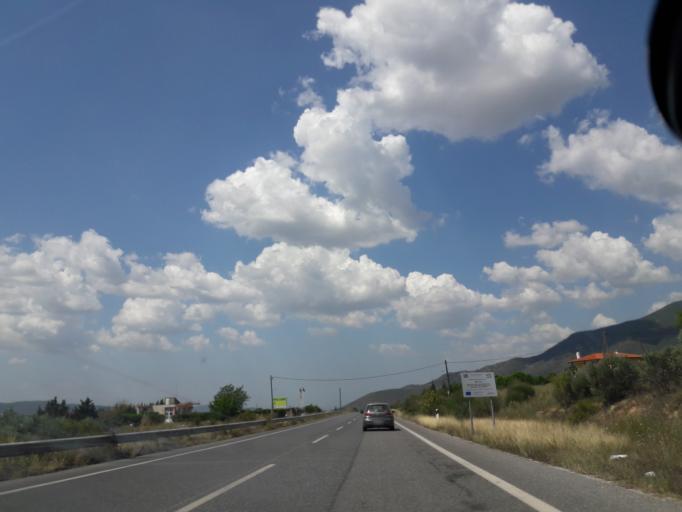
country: GR
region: Central Macedonia
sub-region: Nomos Chalkidikis
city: Galatista
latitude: 40.4651
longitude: 23.2611
